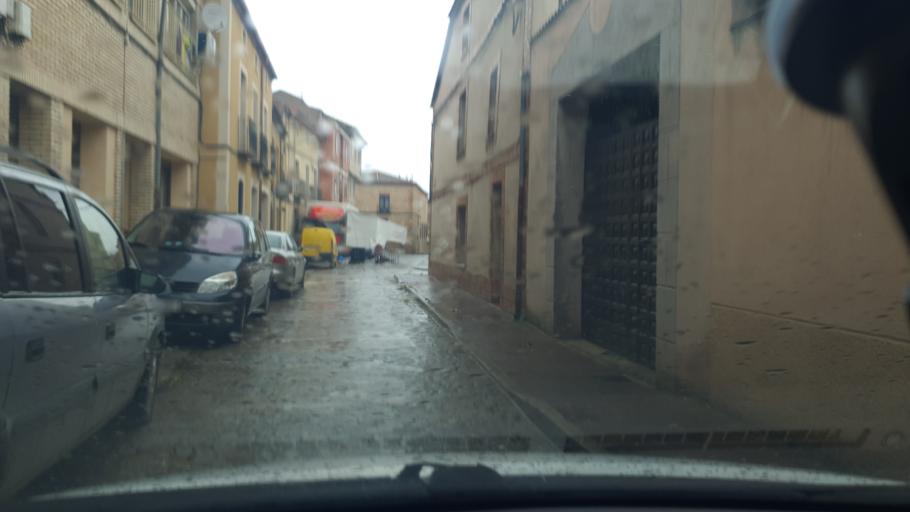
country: ES
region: Castille and Leon
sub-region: Provincia de Segovia
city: Carbonero el Mayor
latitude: 41.1218
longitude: -4.2653
